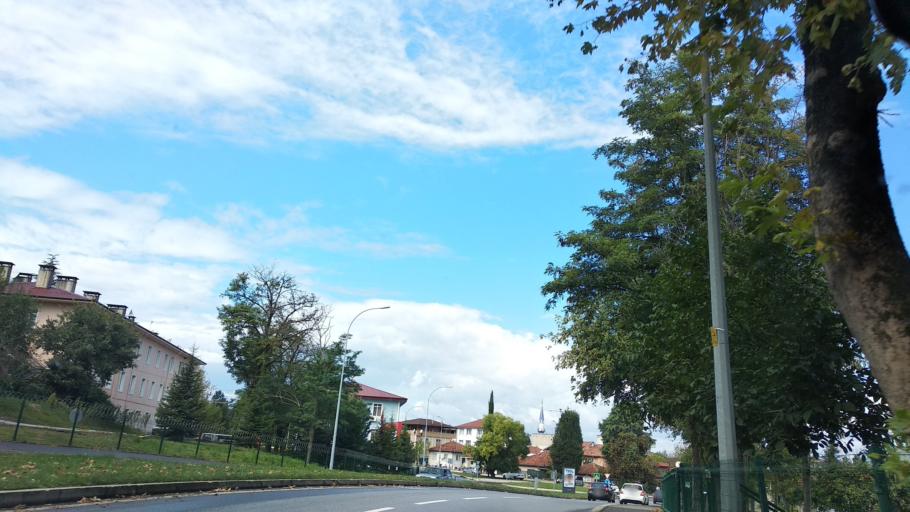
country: TR
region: Sakarya
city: Adapazari
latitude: 40.7567
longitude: 30.3741
